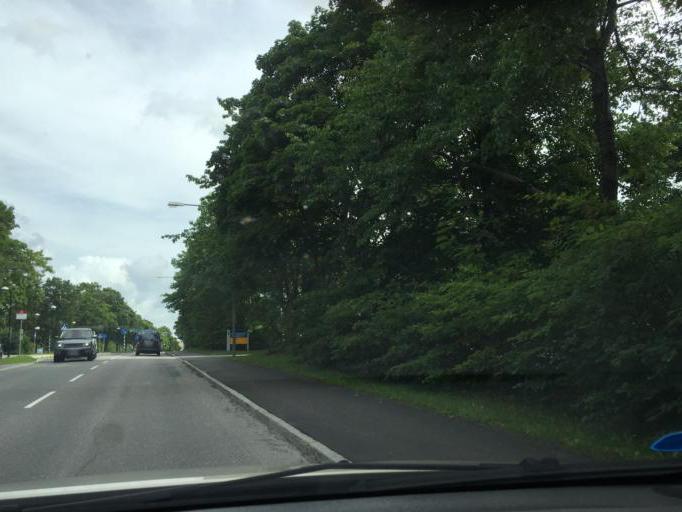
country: SE
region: Stockholm
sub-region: Stockholms Kommun
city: Bromma
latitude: 59.3567
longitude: 17.8891
